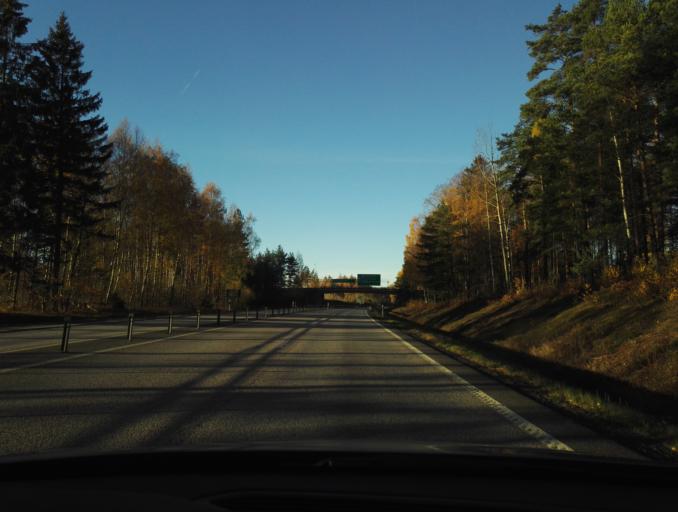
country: SE
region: Kronoberg
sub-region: Vaxjo Kommun
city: Vaexjoe
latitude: 56.8935
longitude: 14.7713
